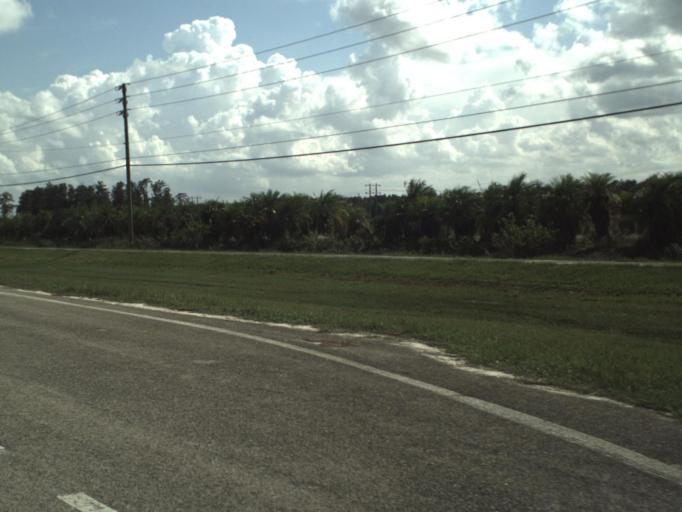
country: US
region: Florida
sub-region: Palm Beach County
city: Villages of Oriole
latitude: 26.5074
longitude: -80.2053
